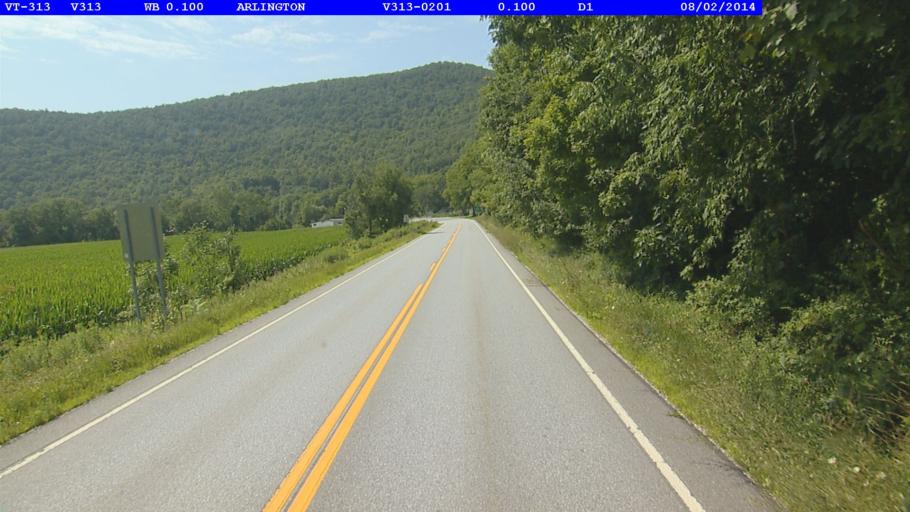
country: US
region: Vermont
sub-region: Bennington County
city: Arlington
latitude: 43.1078
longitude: -73.2629
